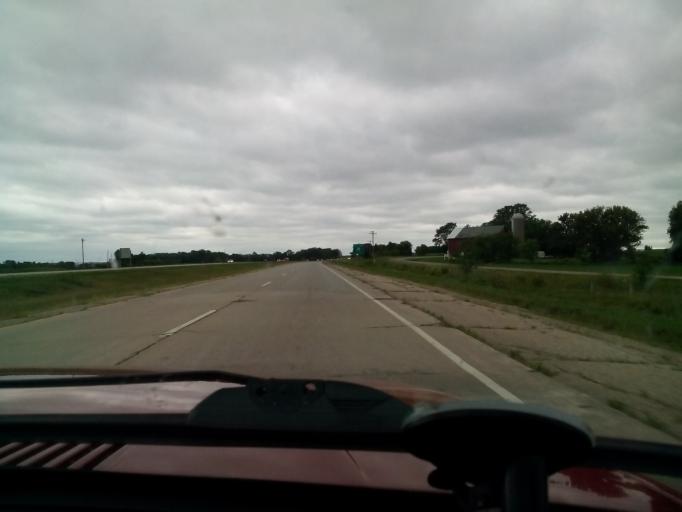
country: US
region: Wisconsin
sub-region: Dane County
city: Marshall
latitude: 43.2555
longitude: -89.1252
